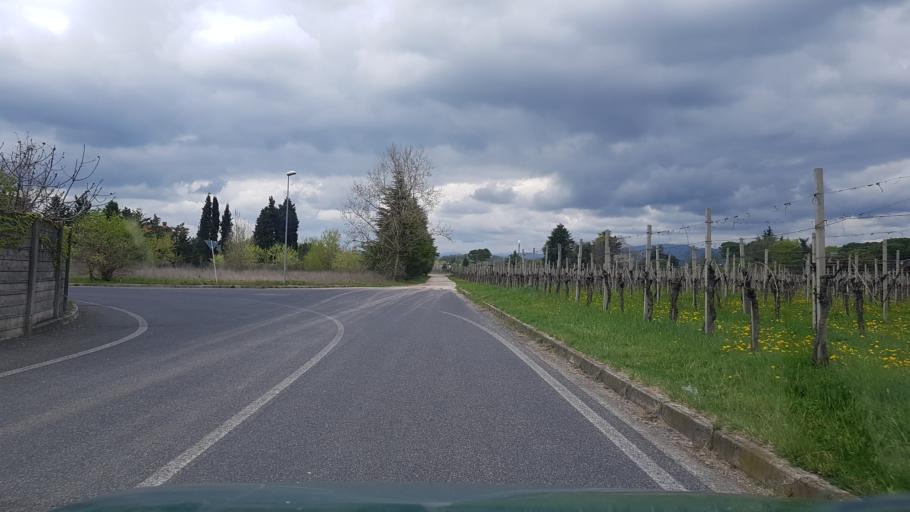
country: IT
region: Friuli Venezia Giulia
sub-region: Provincia di Gorizia
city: Mossa
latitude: 45.9310
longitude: 13.5531
